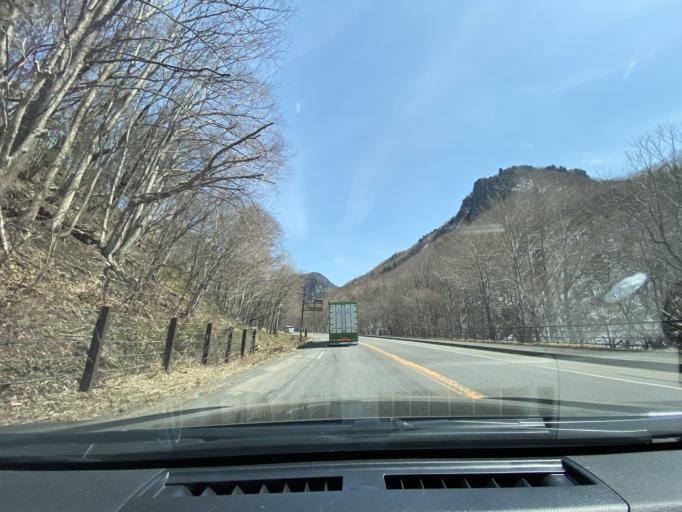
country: JP
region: Hokkaido
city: Kamikawa
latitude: 43.7259
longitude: 142.9574
